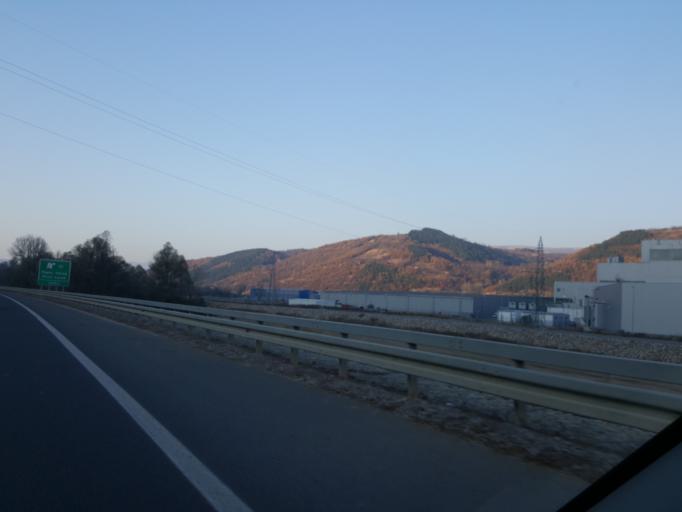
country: RS
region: Central Serbia
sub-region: Pirotski Okrug
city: Pirot
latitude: 43.1731
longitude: 22.5726
